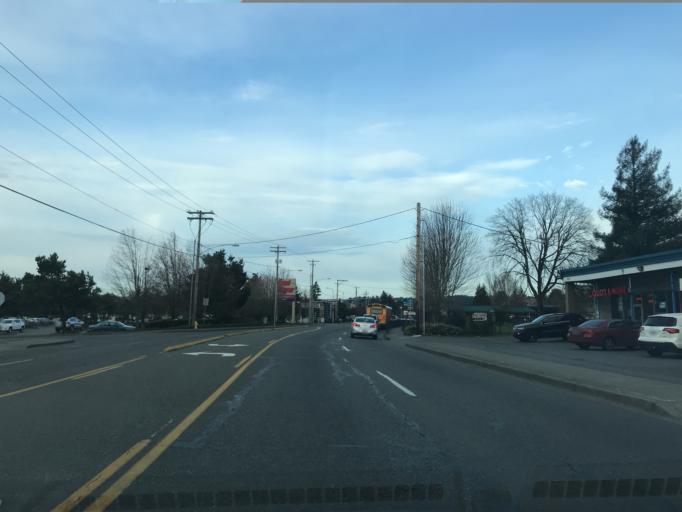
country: US
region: Washington
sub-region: King County
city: Auburn
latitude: 47.3144
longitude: -122.2245
